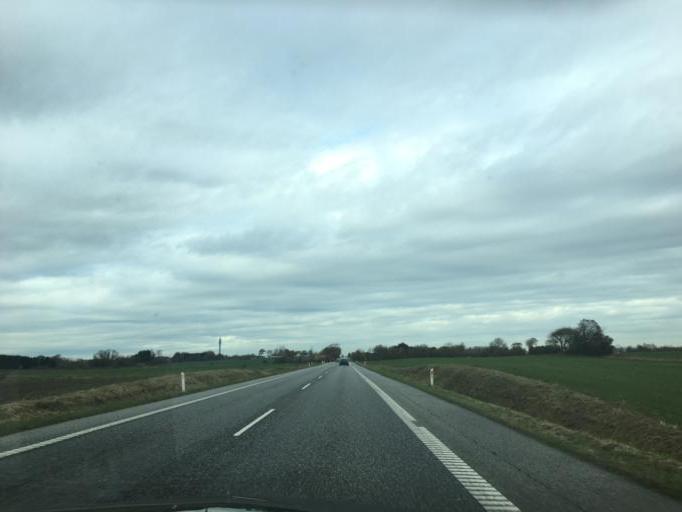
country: DK
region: South Denmark
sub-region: Vejle Kommune
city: Vejle
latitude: 55.6420
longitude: 9.4984
